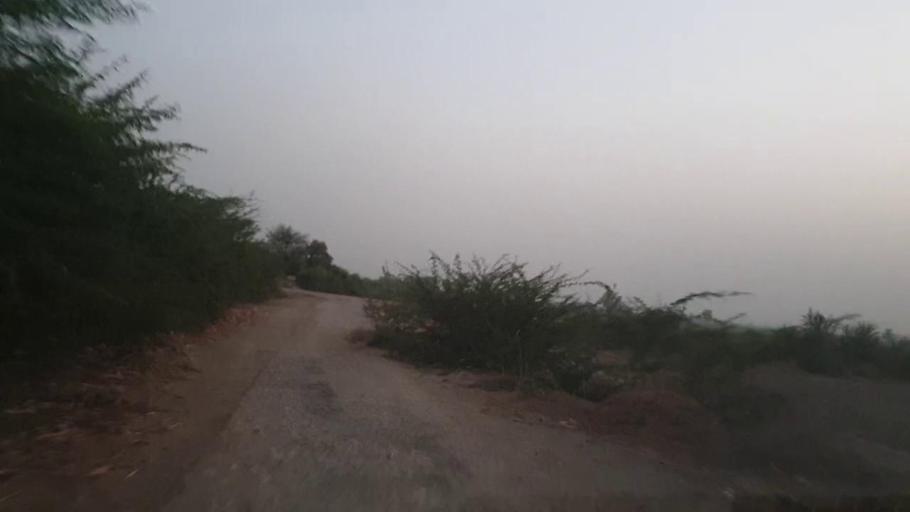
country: PK
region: Sindh
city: Nabisar
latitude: 25.0834
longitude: 69.5698
